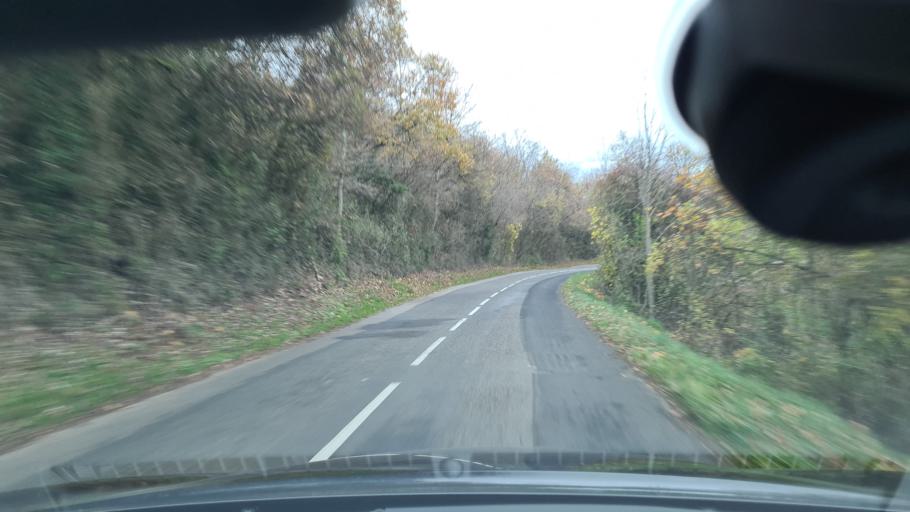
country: FR
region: Rhone-Alpes
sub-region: Departement du Rhone
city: Limonest
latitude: 45.8506
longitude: 4.7828
